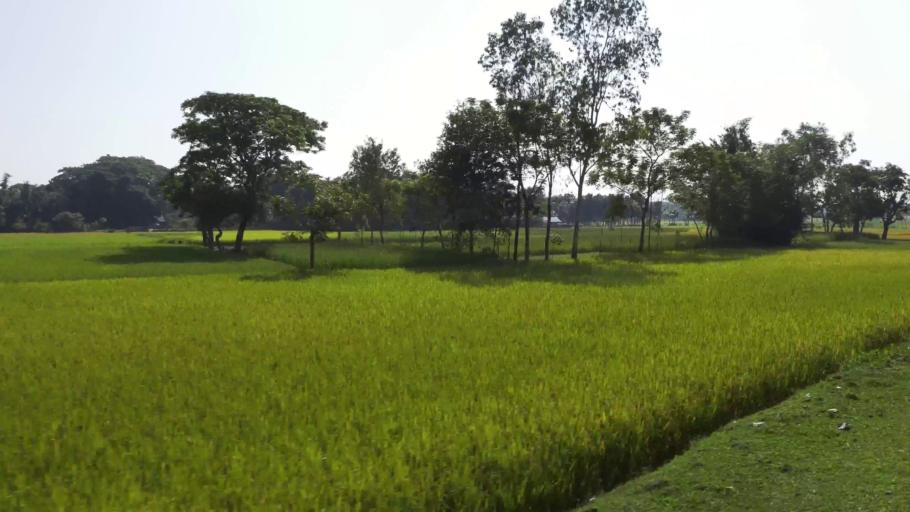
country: BD
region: Dhaka
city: Gafargaon
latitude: 24.5762
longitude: 90.5080
